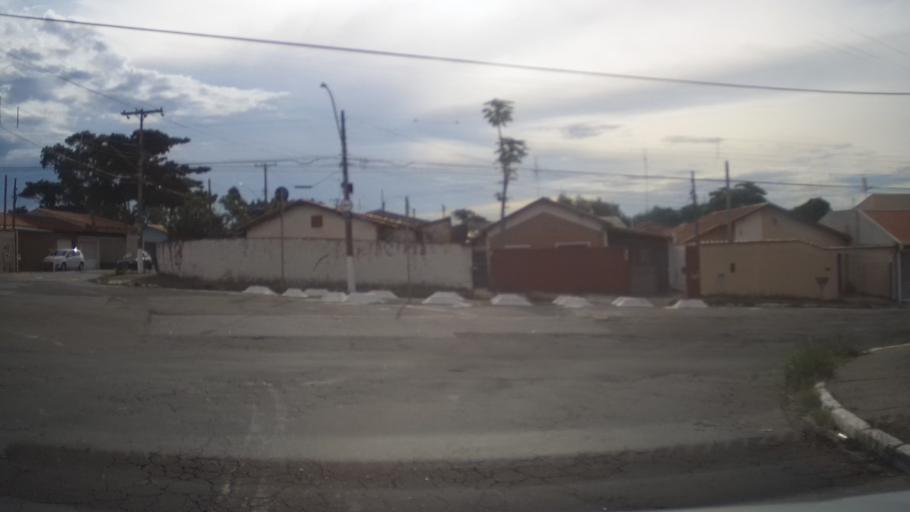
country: BR
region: Sao Paulo
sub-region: Campinas
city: Campinas
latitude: -22.9080
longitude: -47.1197
